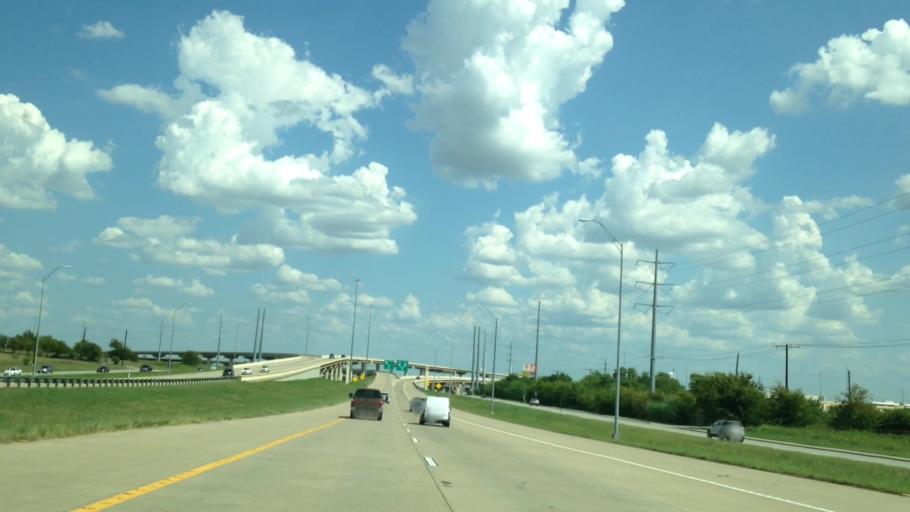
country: US
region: Texas
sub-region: Travis County
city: Pflugerville
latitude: 30.4774
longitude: -97.6005
